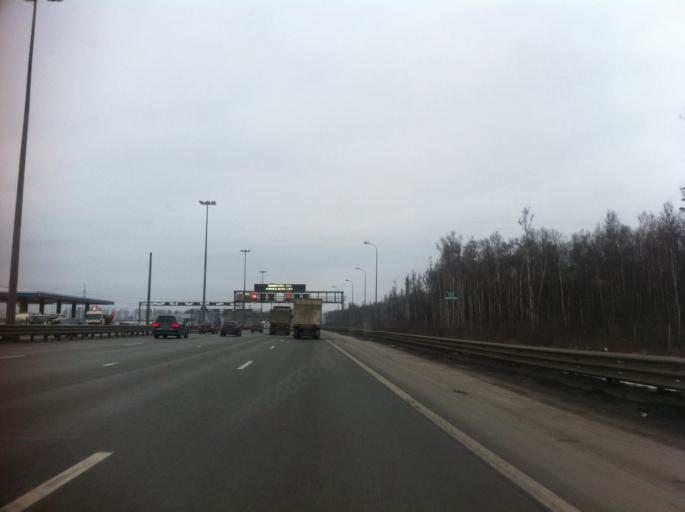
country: RU
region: Leningrad
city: Rybatskoye
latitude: 59.8711
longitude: 30.5318
